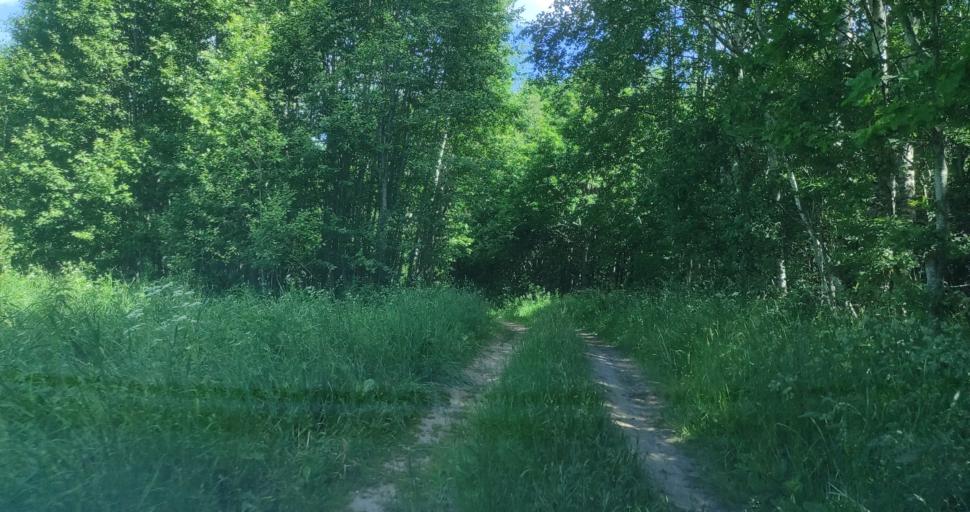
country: LV
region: Aizpute
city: Aizpute
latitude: 56.8616
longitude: 21.7291
